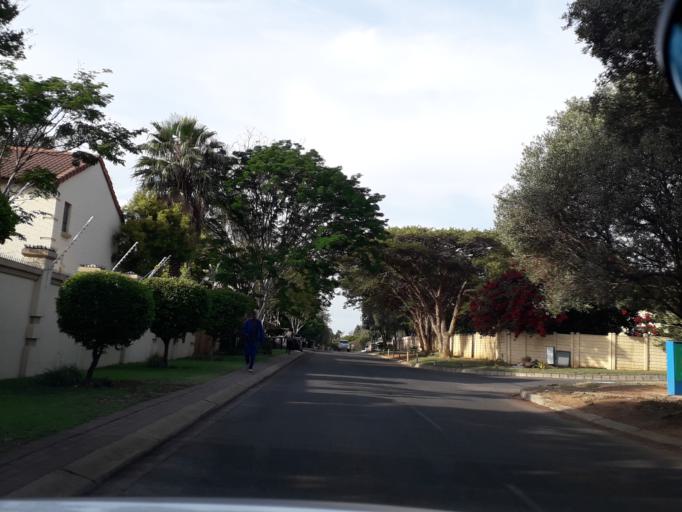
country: ZA
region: Gauteng
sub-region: City of Johannesburg Metropolitan Municipality
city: Diepsloot
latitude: -26.0319
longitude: 27.9909
